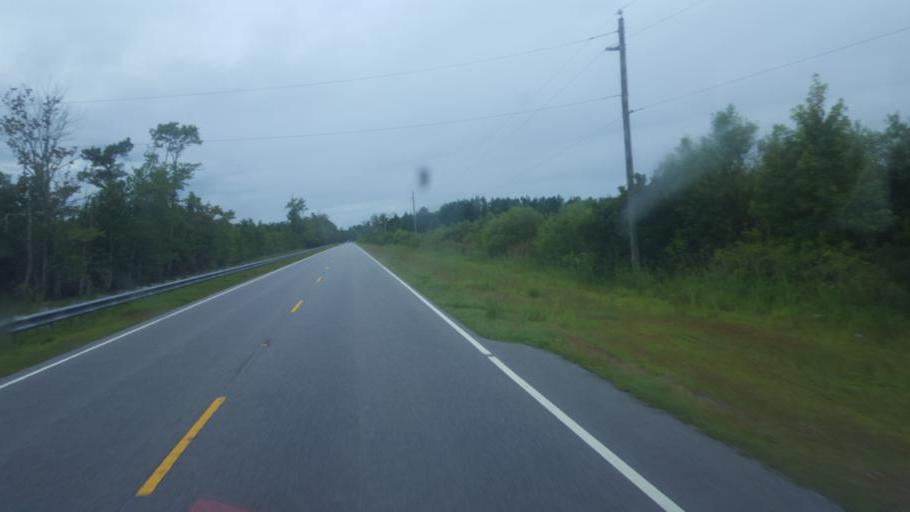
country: US
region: North Carolina
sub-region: Tyrrell County
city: Columbia
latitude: 35.9061
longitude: -76.0995
